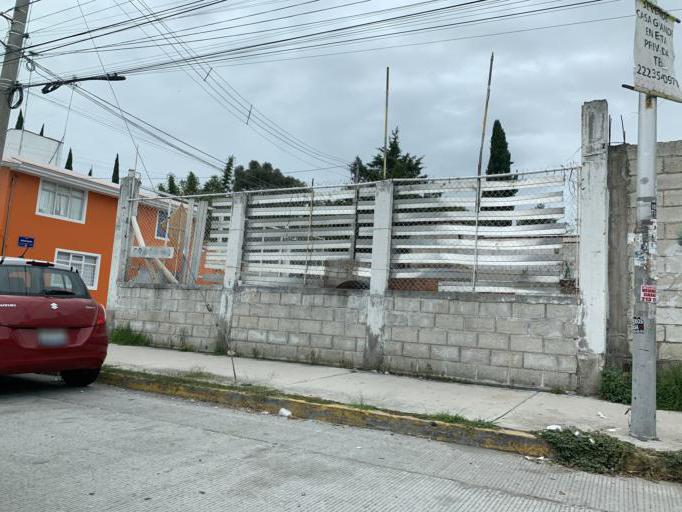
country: MX
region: Puebla
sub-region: Puebla
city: Articulo Primero Constitucional
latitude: 18.9950
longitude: -98.1976
